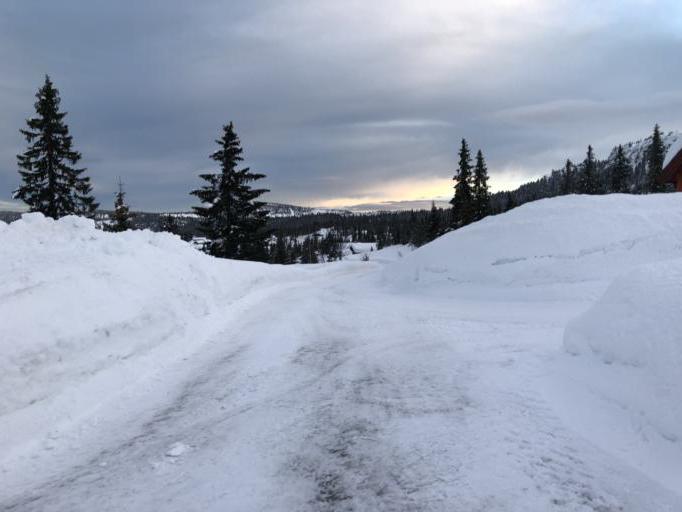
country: NO
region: Oppland
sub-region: Gausdal
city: Segalstad bru
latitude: 61.3296
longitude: 10.0532
